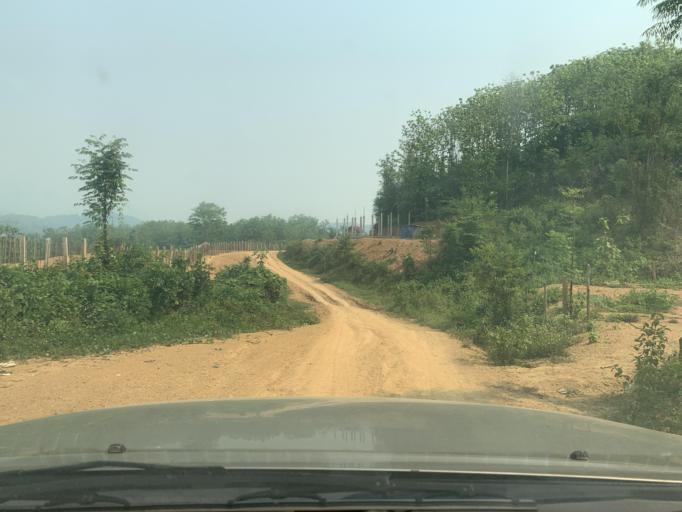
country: LA
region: Louangphabang
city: Xiang Ngeun
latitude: 19.7983
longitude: 102.2012
